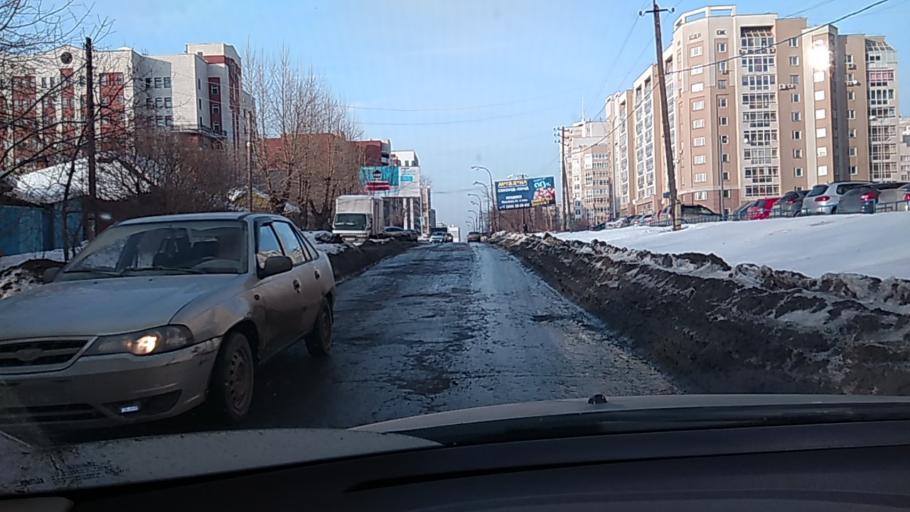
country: RU
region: Sverdlovsk
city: Yekaterinburg
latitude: 56.8036
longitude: 60.6000
